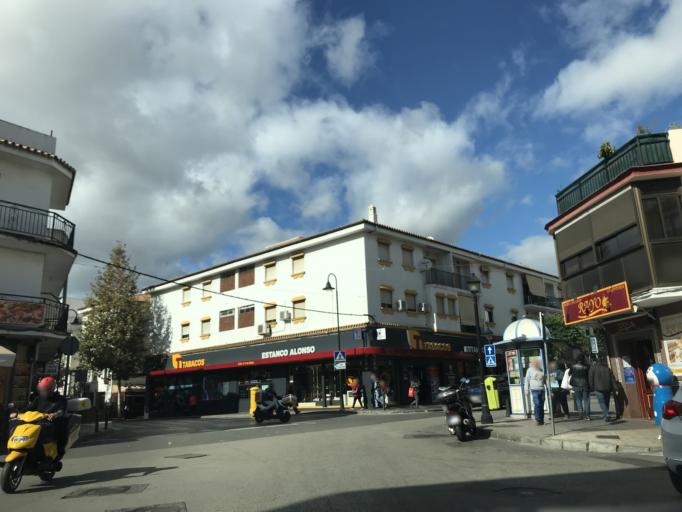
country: ES
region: Andalusia
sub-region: Provincia de Malaga
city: Fuengirola
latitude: 36.5403
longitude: -4.6304
